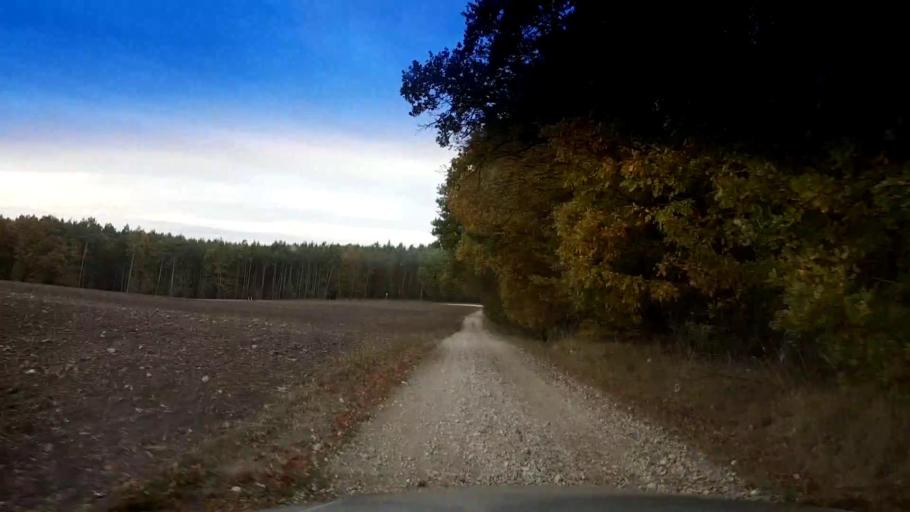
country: DE
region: Bavaria
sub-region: Upper Franconia
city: Priesendorf
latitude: 49.9182
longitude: 10.7208
